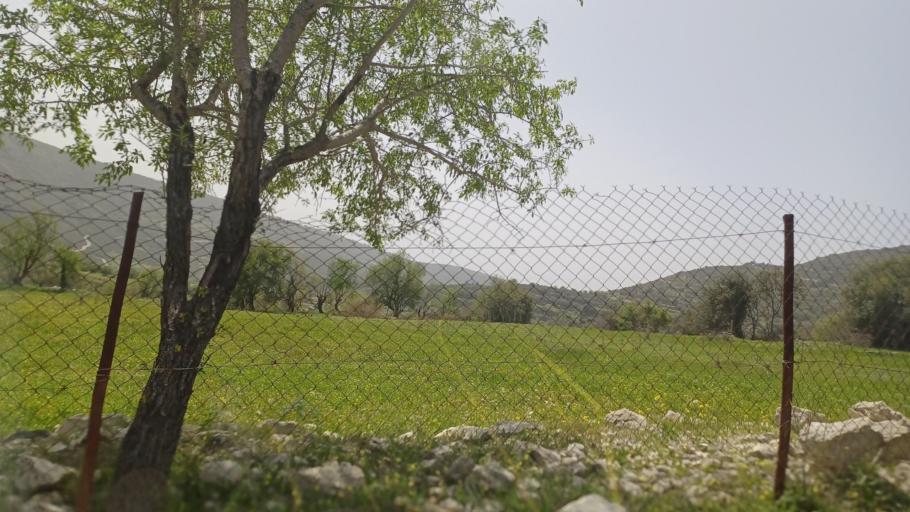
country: CY
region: Limassol
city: Pachna
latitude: 34.7837
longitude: 32.7443
